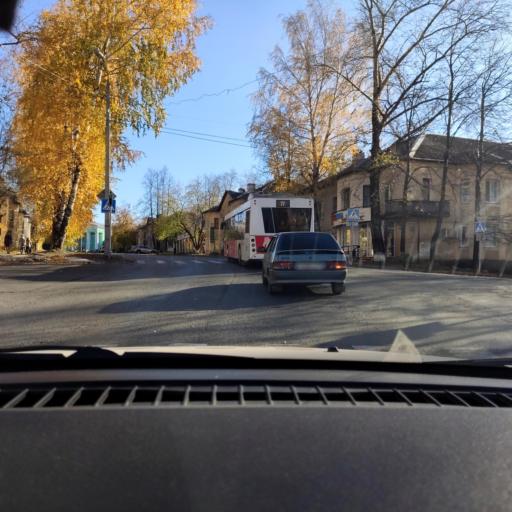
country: RU
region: Perm
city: Perm
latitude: 58.1122
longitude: 56.3682
